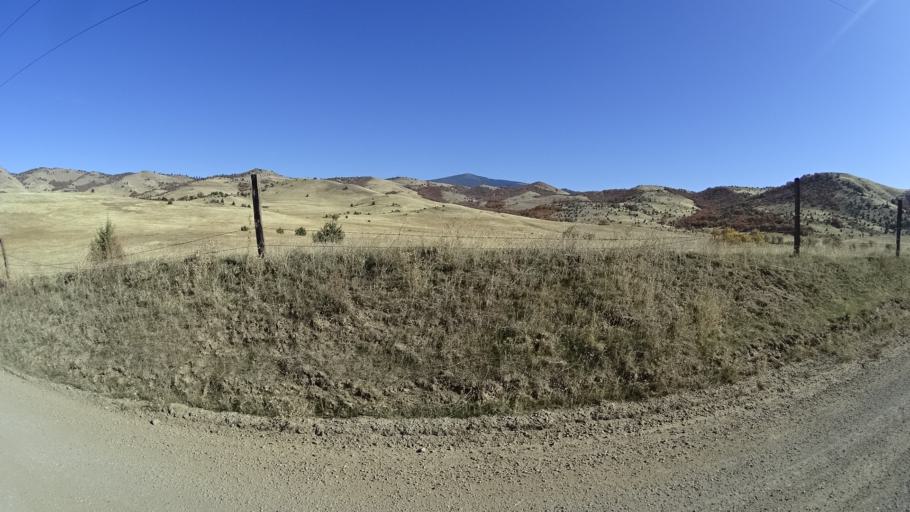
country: US
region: California
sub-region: Siskiyou County
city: Montague
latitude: 41.8164
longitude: -122.3629
